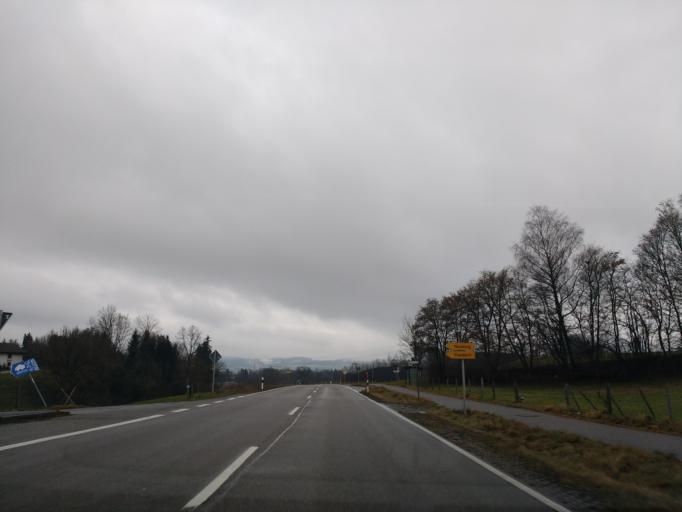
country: DE
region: Bavaria
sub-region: Swabia
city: Neuburg
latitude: 47.7741
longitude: 10.3465
